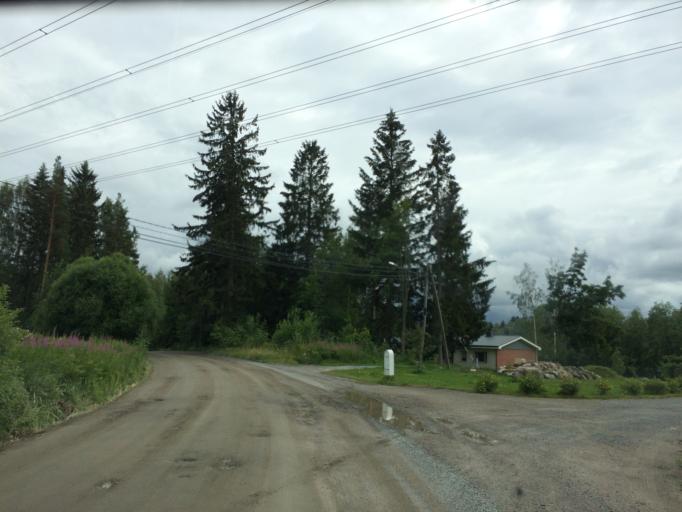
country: FI
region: Haeme
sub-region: Haemeenlinna
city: Haemeenlinna
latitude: 60.9729
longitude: 24.5206
